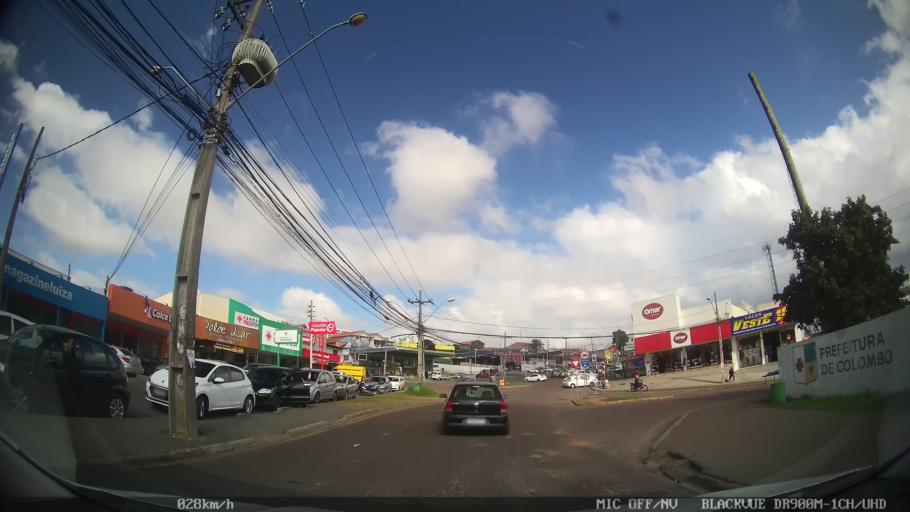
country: BR
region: Parana
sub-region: Pinhais
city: Pinhais
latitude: -25.3674
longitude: -49.1853
